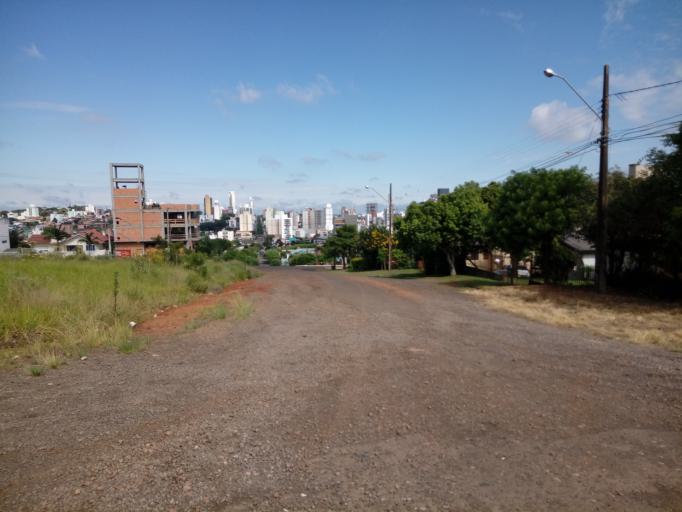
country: BR
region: Santa Catarina
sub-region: Chapeco
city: Chapeco
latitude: -27.1059
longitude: -52.5988
